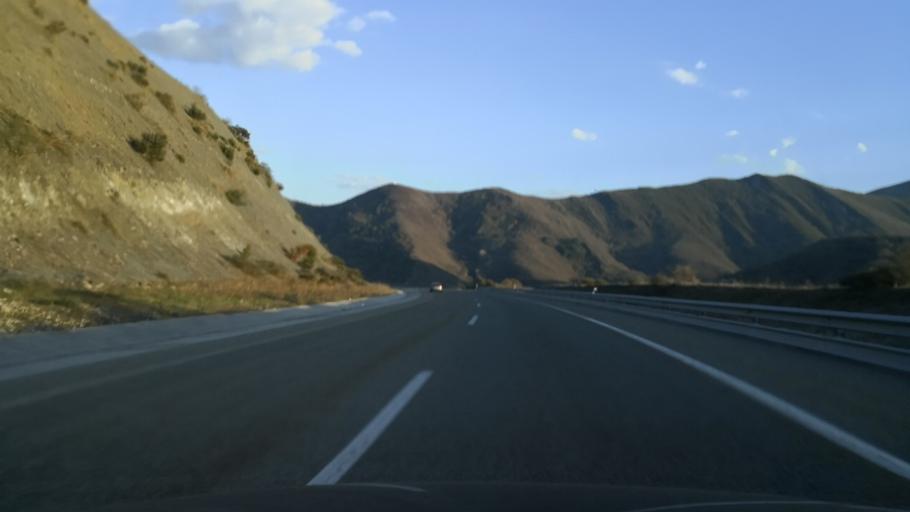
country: ES
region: Castille and Leon
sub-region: Provincia de Leon
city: Vega de Valcarce
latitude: 42.6776
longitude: -6.9886
